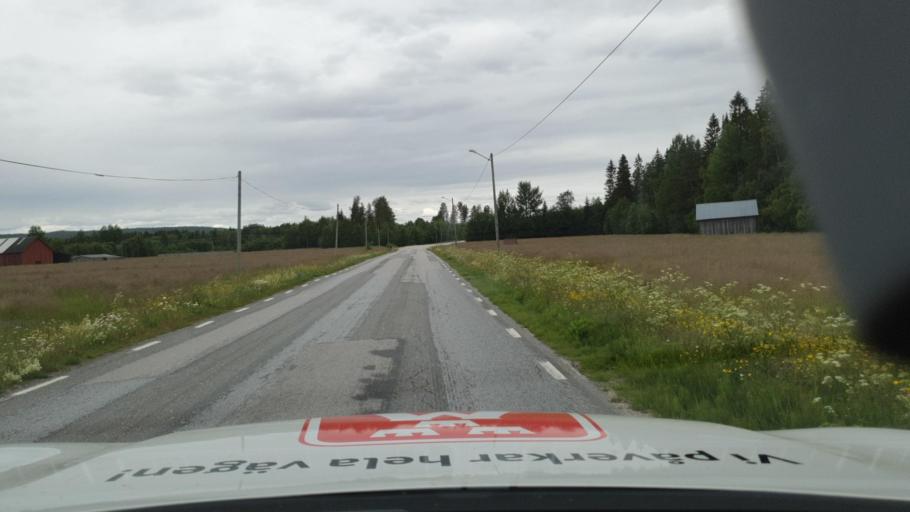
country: SE
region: Vaesterbotten
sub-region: Nordmalings Kommun
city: Nordmaling
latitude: 63.5302
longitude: 19.4069
